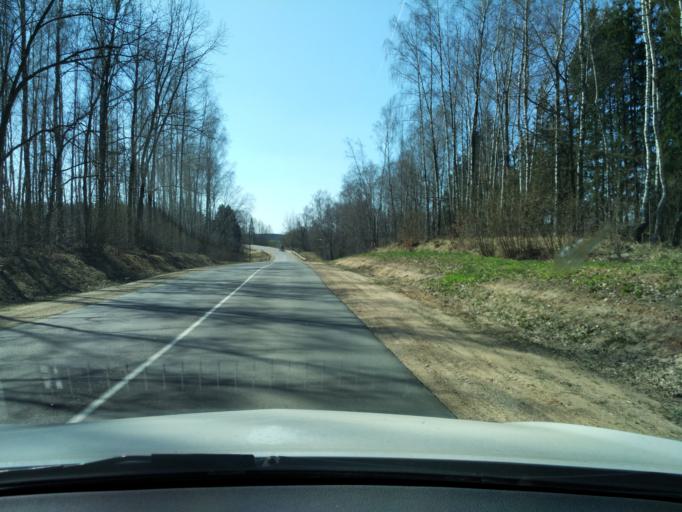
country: BY
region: Minsk
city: Slabada
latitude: 53.9902
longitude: 27.9625
